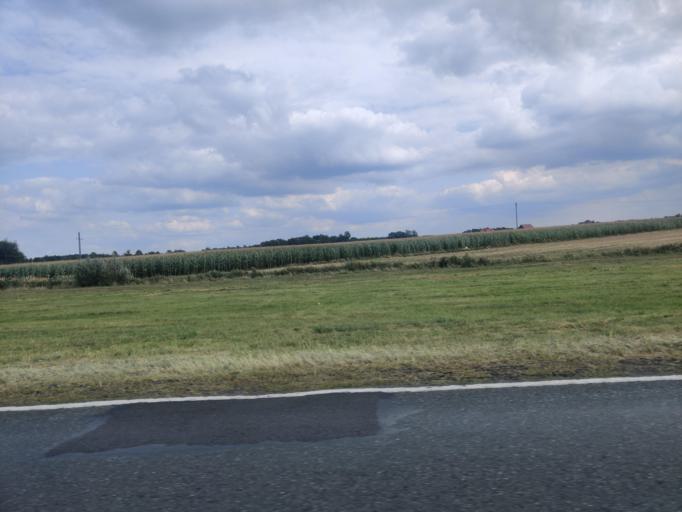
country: PL
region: Greater Poland Voivodeship
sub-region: Powiat koninski
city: Rychwal
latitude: 52.1298
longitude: 18.1800
